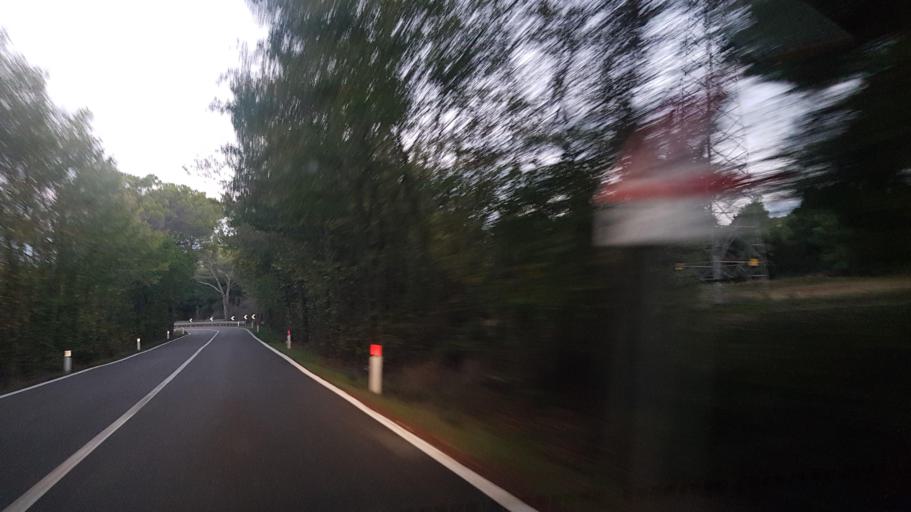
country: IT
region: Basilicate
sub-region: Provincia di Matera
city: Matera
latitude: 40.6766
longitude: 16.6626
